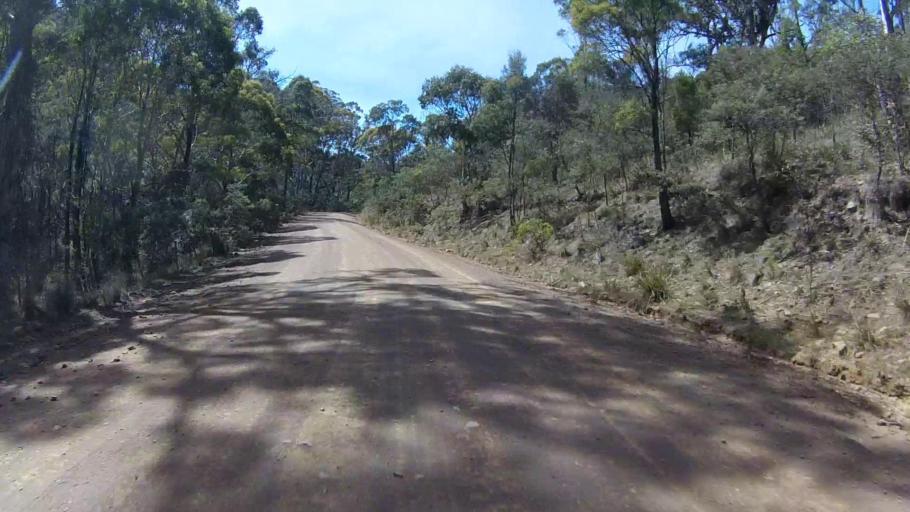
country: AU
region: Tasmania
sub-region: Sorell
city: Sorell
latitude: -42.6421
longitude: 147.7360
